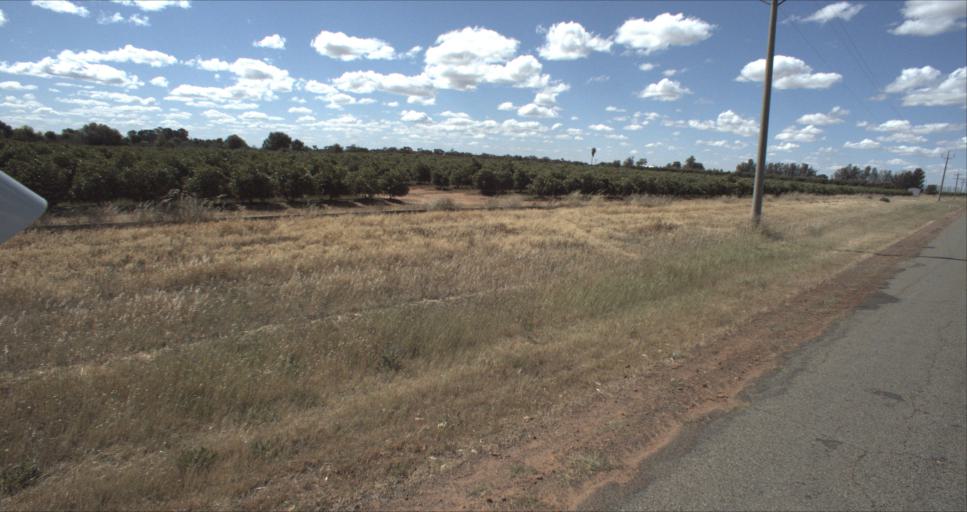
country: AU
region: New South Wales
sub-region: Leeton
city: Leeton
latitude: -34.5150
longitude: 146.2388
